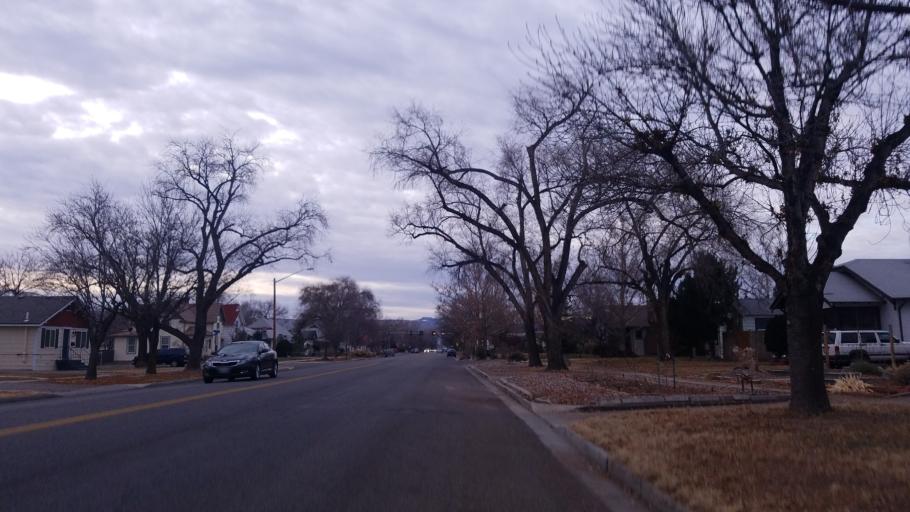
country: US
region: Colorado
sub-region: Mesa County
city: Grand Junction
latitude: 39.0704
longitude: -108.5499
